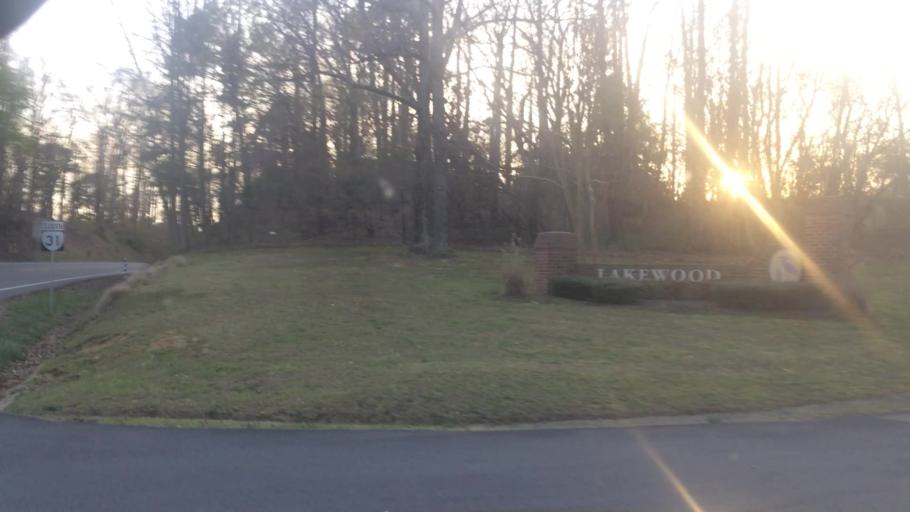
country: US
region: Virginia
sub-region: James City County
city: Williamsburg
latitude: 37.2369
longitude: -76.7486
